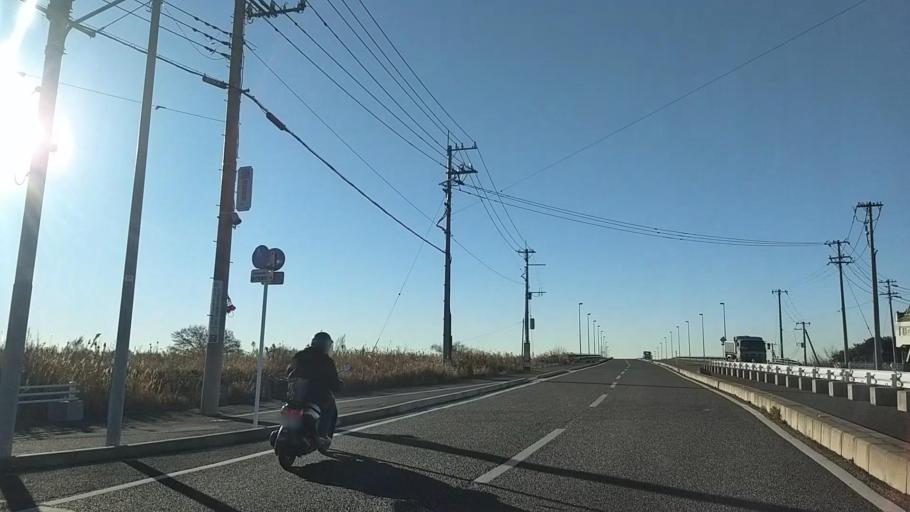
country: JP
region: Chiba
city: Kisarazu
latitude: 35.4229
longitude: 139.9197
